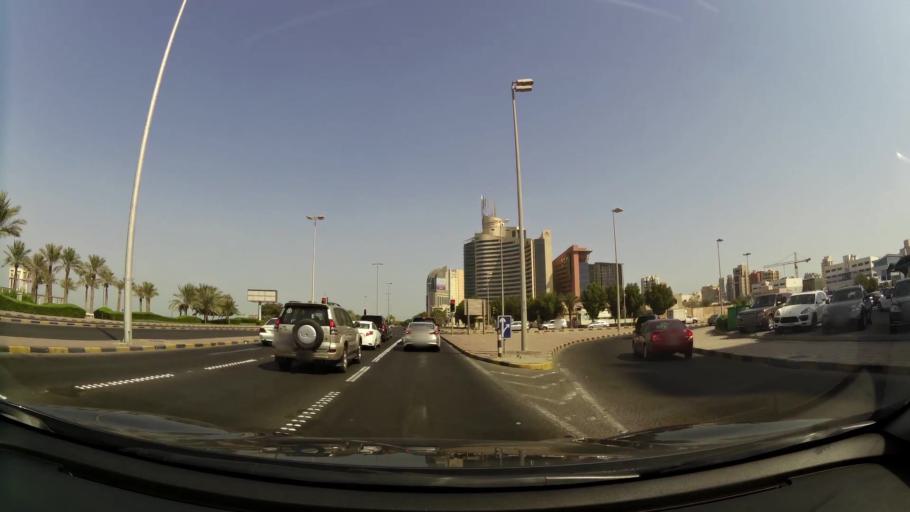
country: KW
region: Muhafazat Hawalli
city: As Salimiyah
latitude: 29.3456
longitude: 48.0804
